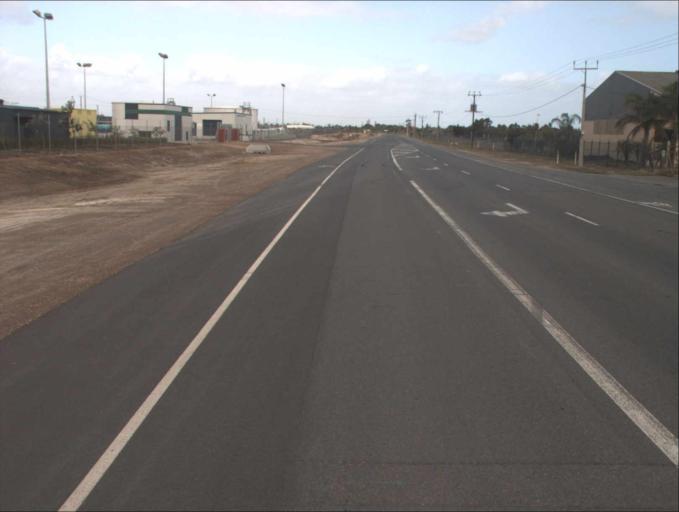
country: AU
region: South Australia
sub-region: Port Adelaide Enfield
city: Birkenhead
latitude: -34.7747
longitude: 138.5016
